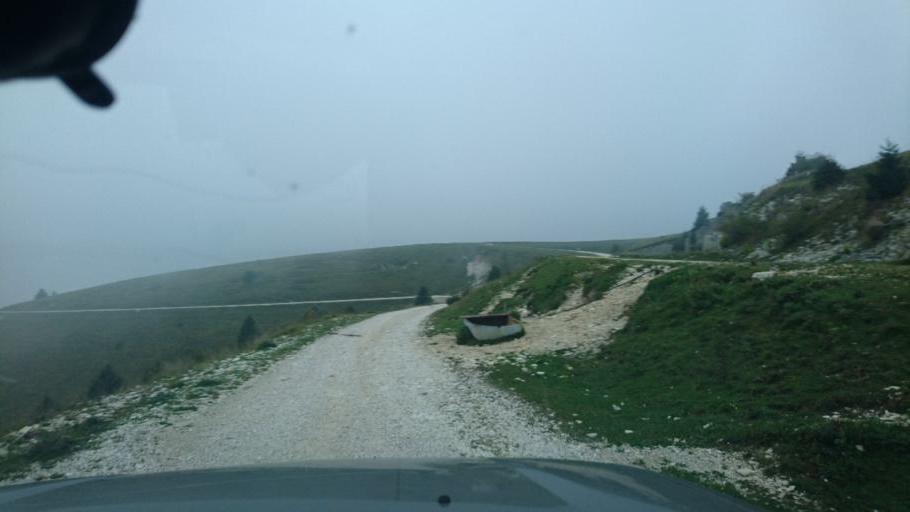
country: IT
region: Veneto
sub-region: Provincia di Vicenza
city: Enego
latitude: 45.9395
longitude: 11.6624
